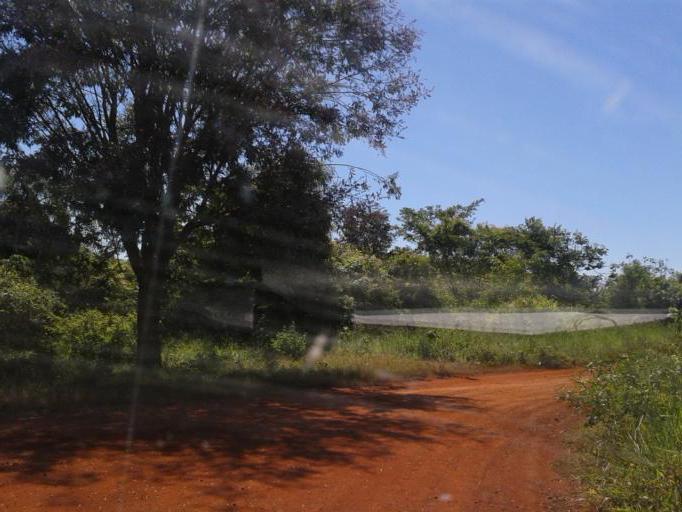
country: BR
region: Minas Gerais
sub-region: Capinopolis
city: Capinopolis
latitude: -18.6268
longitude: -49.6167
